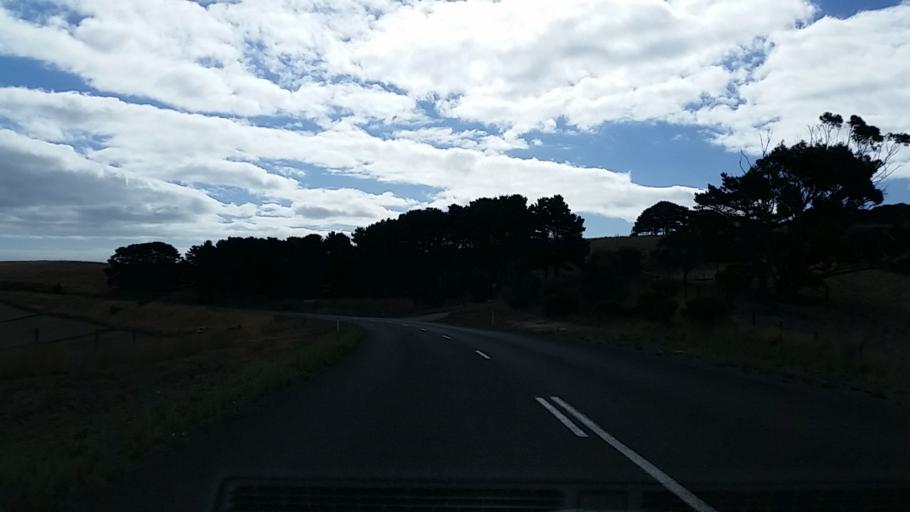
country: AU
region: South Australia
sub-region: Yankalilla
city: Normanville
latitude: -35.4119
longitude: 138.3701
